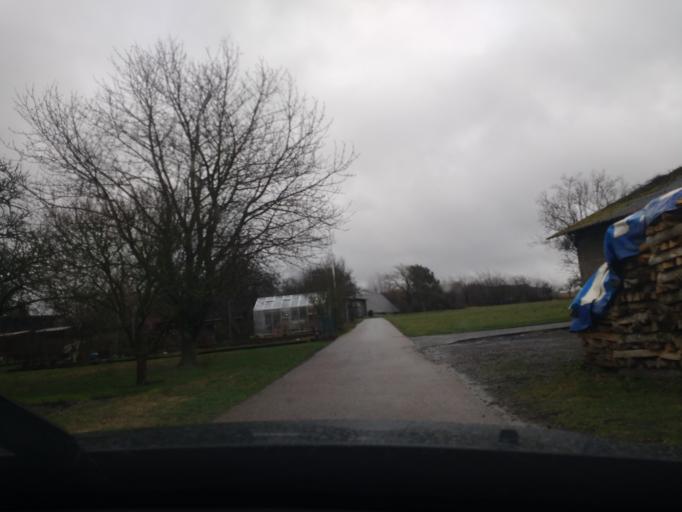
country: DE
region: Rheinland-Pfalz
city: Kleinich
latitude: 49.9143
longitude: 7.1854
